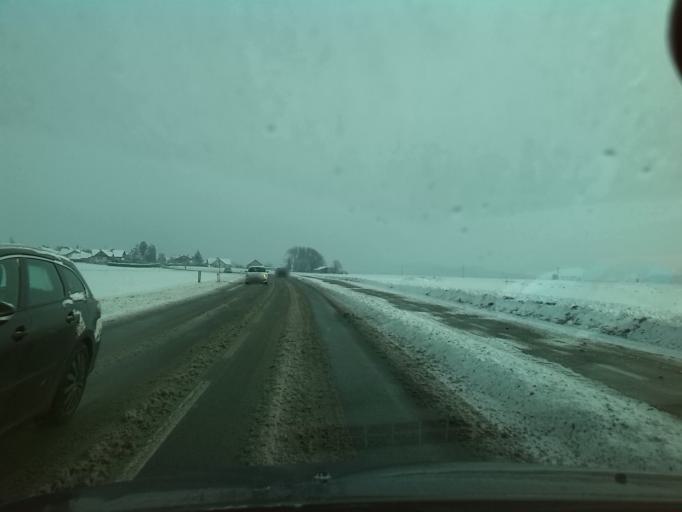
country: SI
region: Komenda
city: Moste
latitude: 46.1965
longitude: 14.5578
